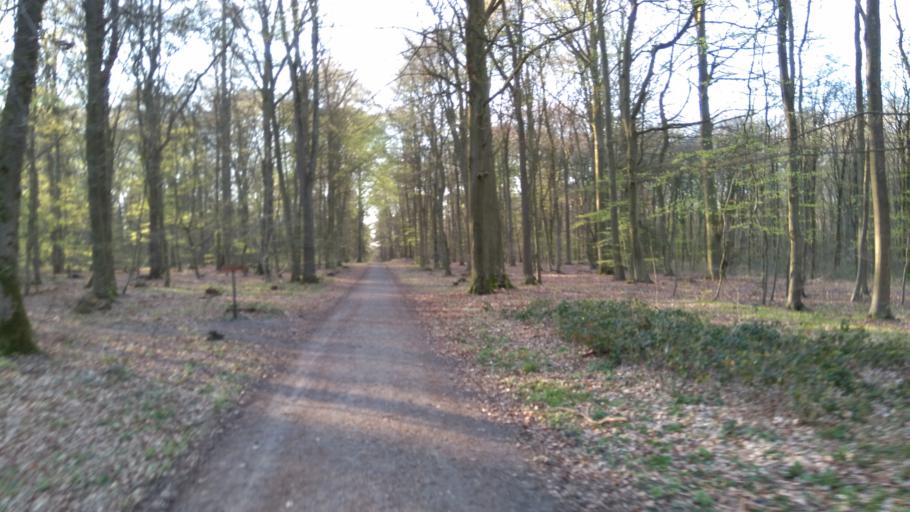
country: DE
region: Lower Saxony
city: Buxtehude
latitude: 53.4735
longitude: 9.6431
